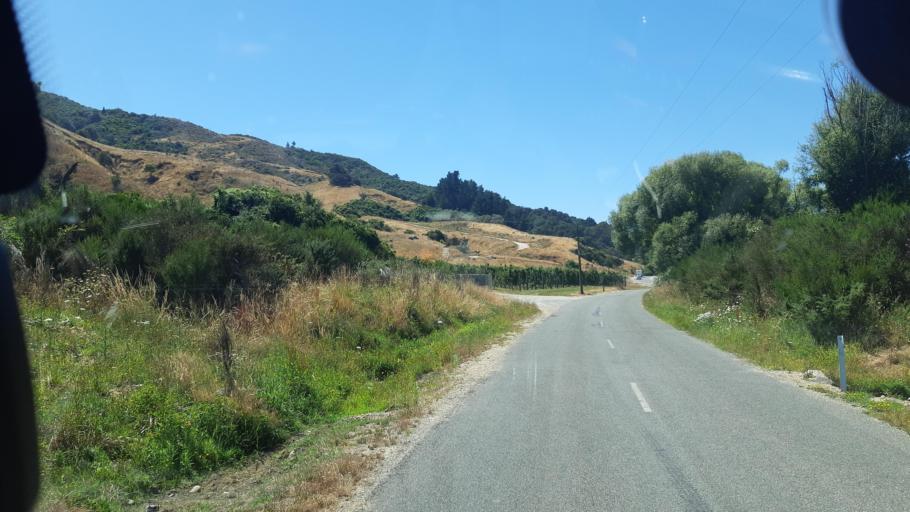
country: NZ
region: Tasman
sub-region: Tasman District
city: Motueka
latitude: -41.0512
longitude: 172.9541
